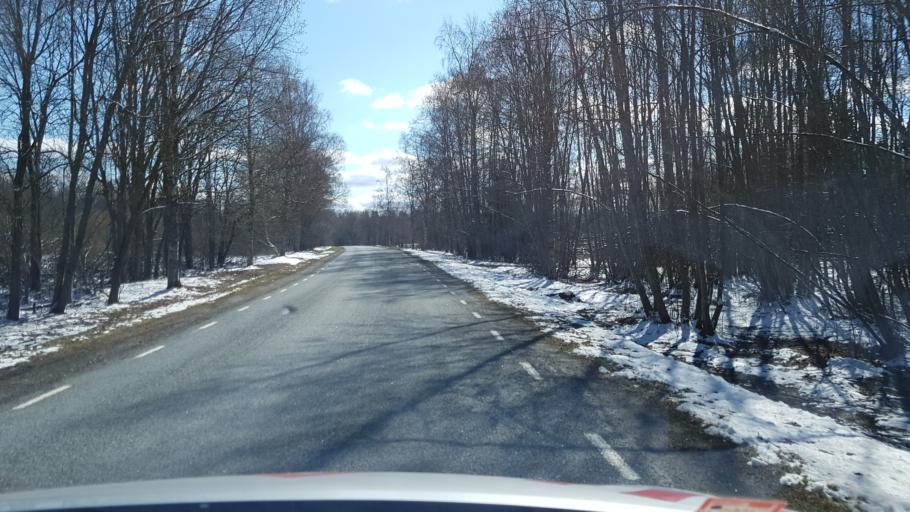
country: EE
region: Laeaene-Virumaa
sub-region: Tapa vald
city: Tapa
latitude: 59.4972
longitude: 25.9718
